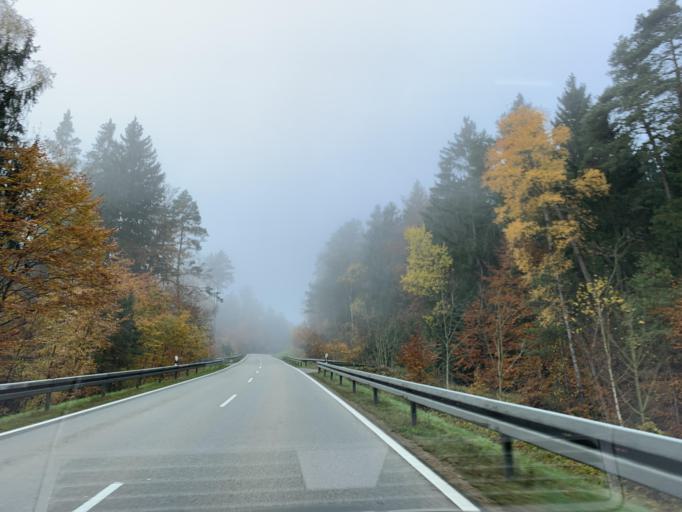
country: DE
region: Bavaria
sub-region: Upper Palatinate
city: Brunn
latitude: 49.2295
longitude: 12.1622
